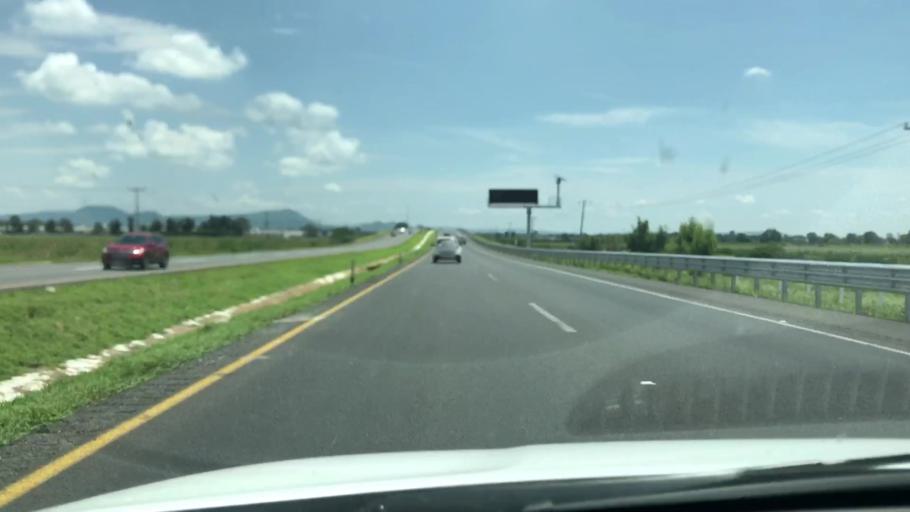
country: MX
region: Guanajuato
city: Irapuato
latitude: 20.6523
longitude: -101.3195
